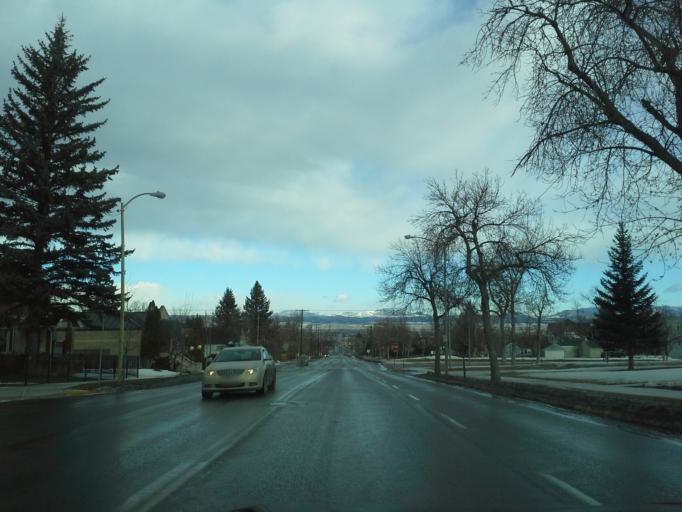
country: US
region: Montana
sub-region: Lewis and Clark County
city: Helena
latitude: 46.5858
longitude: -112.0203
